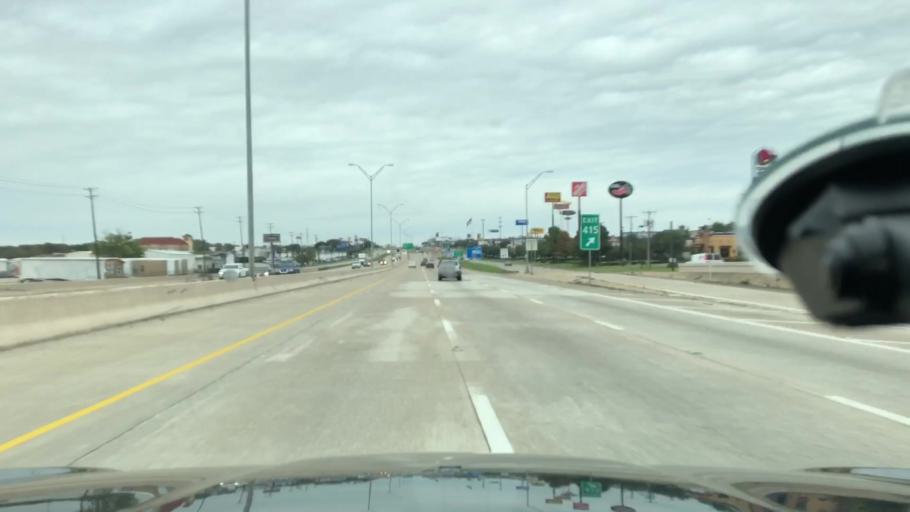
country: US
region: Texas
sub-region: Dallas County
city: DeSoto
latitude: 32.5934
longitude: -96.8224
